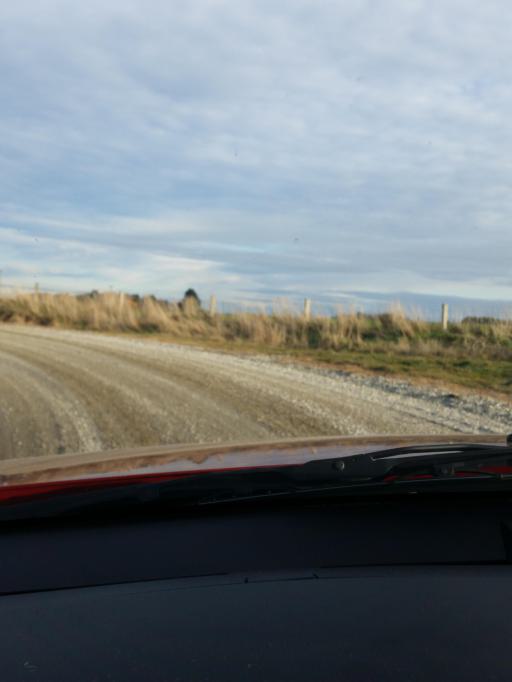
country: NZ
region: Southland
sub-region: Gore District
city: Gore
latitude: -46.2425
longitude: 168.7572
